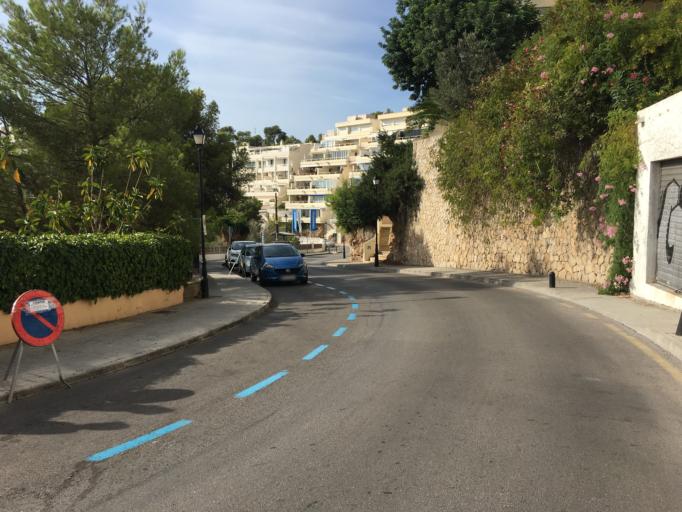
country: ES
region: Balearic Islands
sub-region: Illes Balears
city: Magaluf
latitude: 39.5376
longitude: 2.5902
